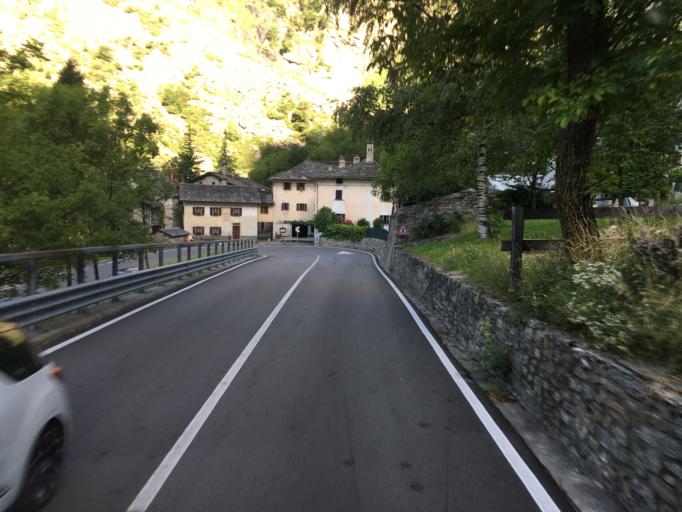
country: IT
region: Lombardy
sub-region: Provincia di Sondrio
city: San Giacomo Filippo
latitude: 46.3680
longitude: 9.3617
